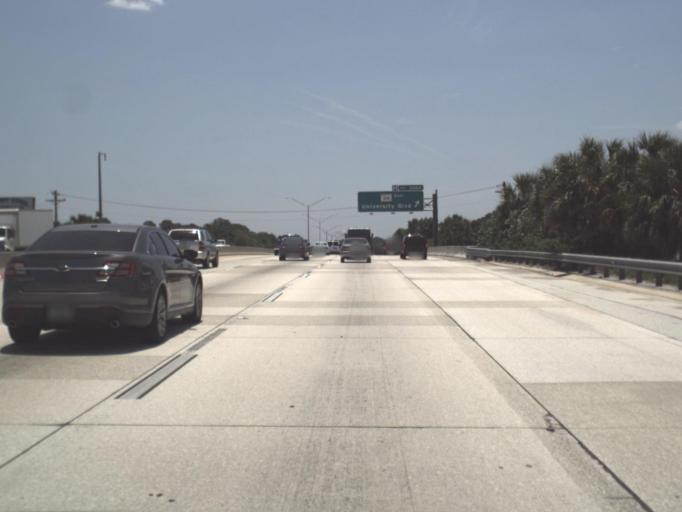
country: US
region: Florida
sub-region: Duval County
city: Jacksonville
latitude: 30.2701
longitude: -81.6128
